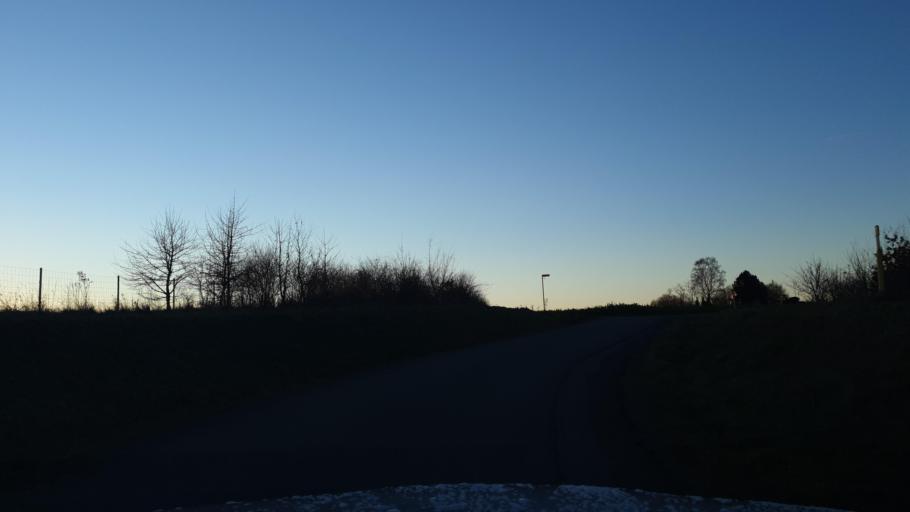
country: DE
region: North Rhine-Westphalia
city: Bad Oeynhausen
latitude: 52.2351
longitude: 8.8242
